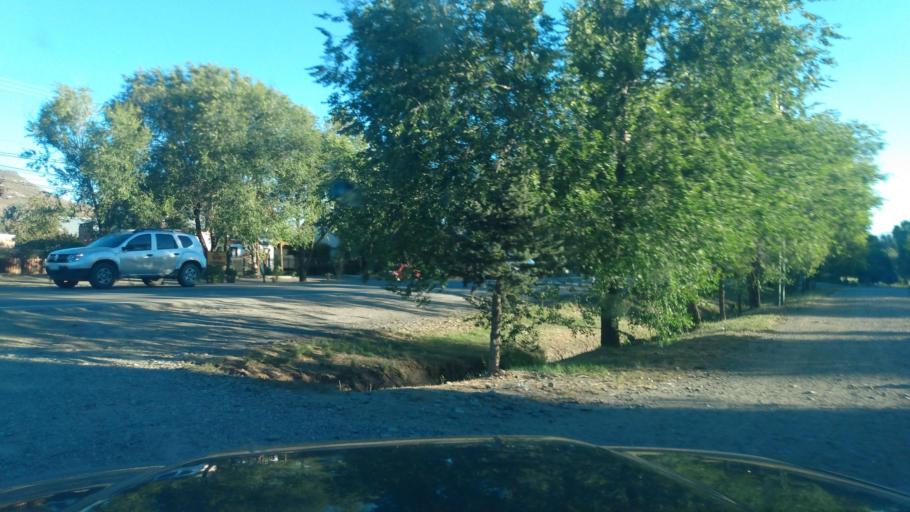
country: AR
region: Neuquen
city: Junin de los Andes
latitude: -39.9571
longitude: -71.0786
